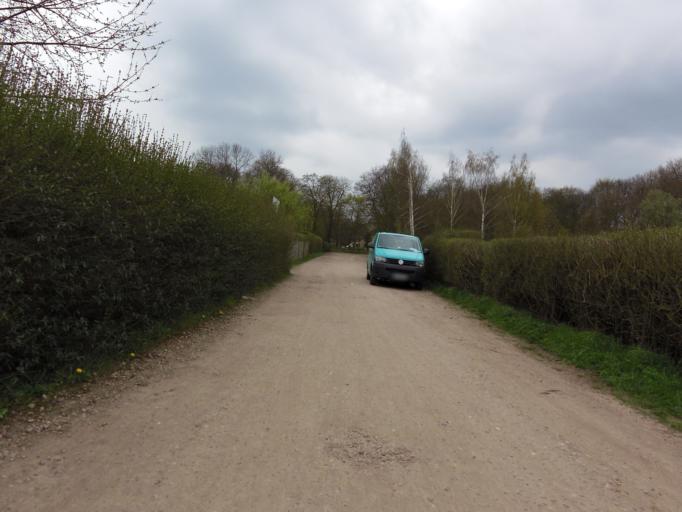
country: DE
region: Thuringia
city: Gotha
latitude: 50.9650
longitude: 10.7152
